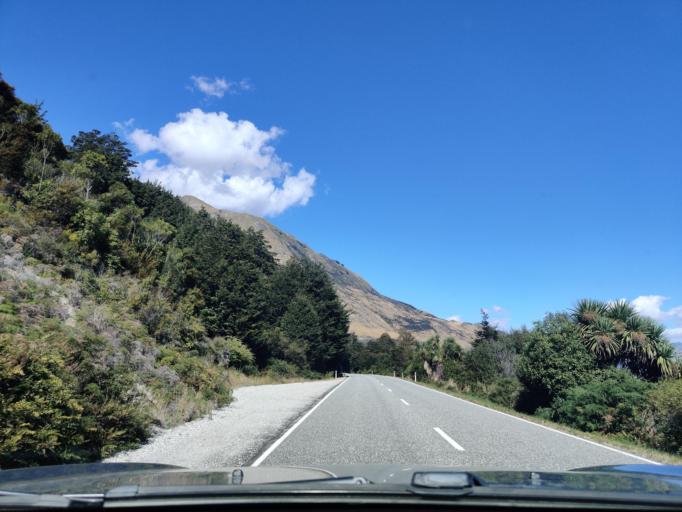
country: NZ
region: Otago
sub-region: Queenstown-Lakes District
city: Queenstown
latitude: -44.9948
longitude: 168.4337
